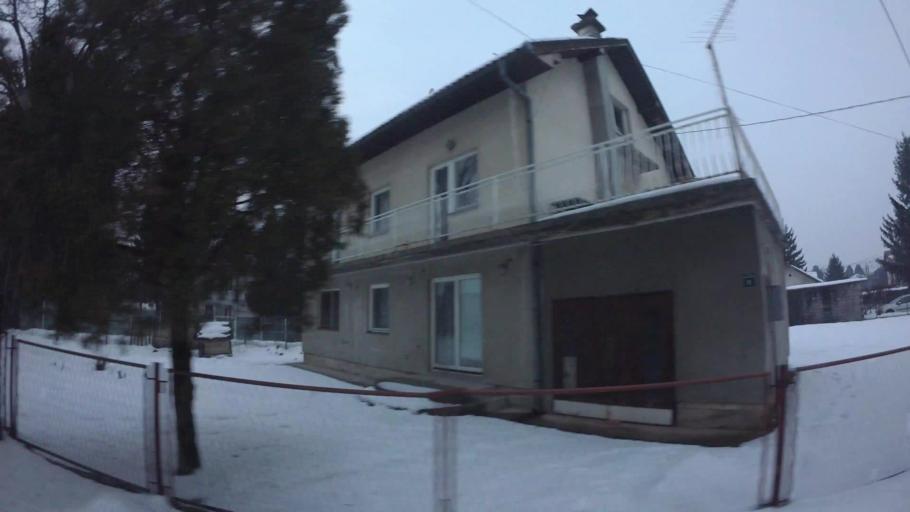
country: BA
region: Federation of Bosnia and Herzegovina
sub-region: Kanton Sarajevo
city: Sarajevo
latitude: 43.8514
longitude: 18.3019
